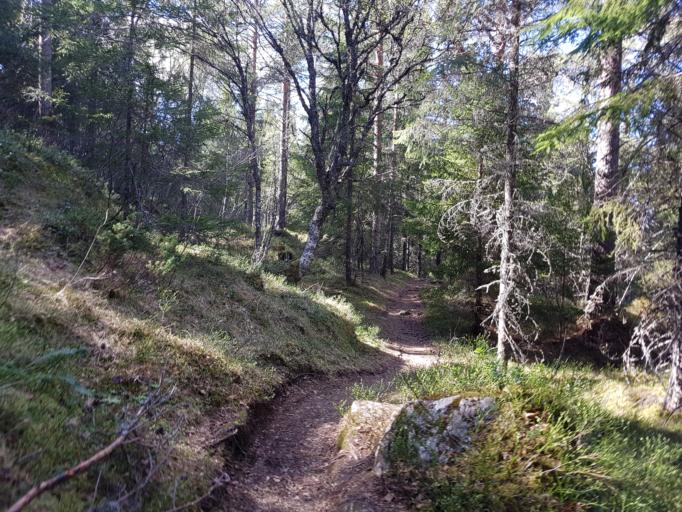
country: NO
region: Sor-Trondelag
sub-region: Trondheim
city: Trondheim
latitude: 63.4427
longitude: 10.3116
